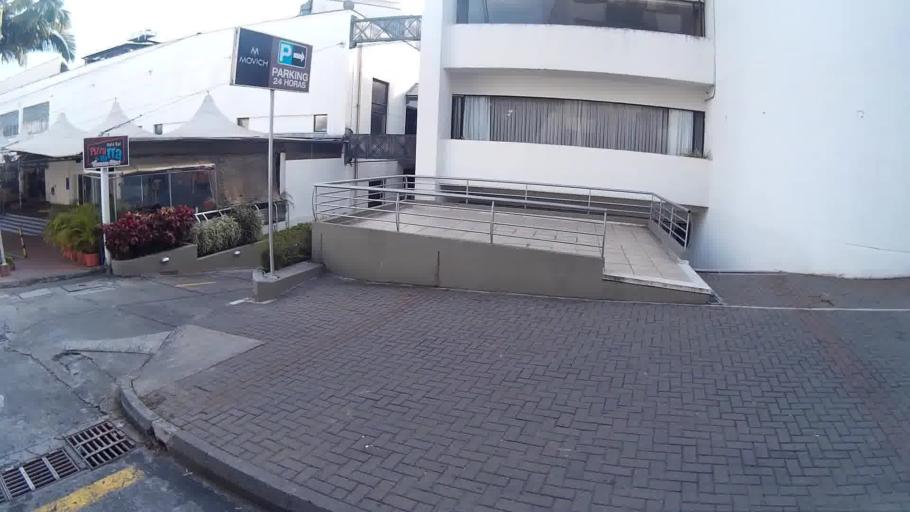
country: CO
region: Risaralda
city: Pereira
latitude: 4.8085
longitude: -75.6913
